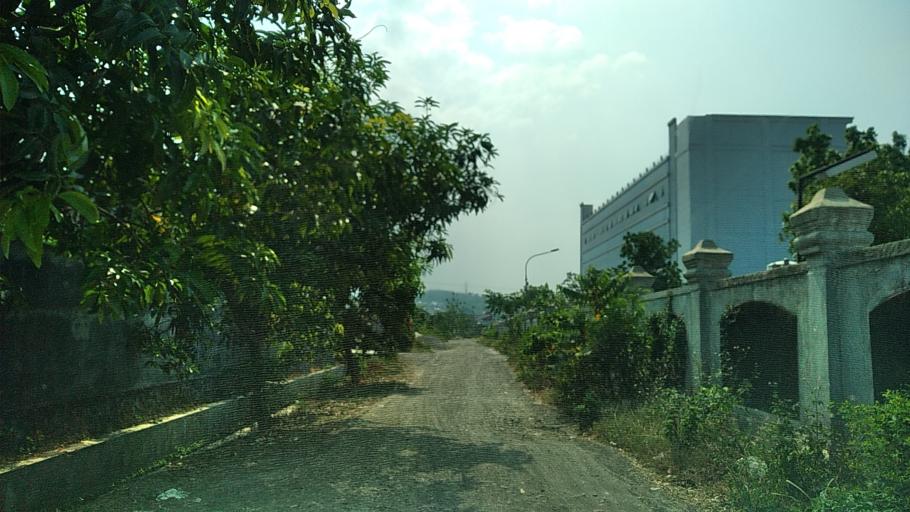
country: ID
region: Central Java
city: Mranggen
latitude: -7.0352
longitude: 110.4666
